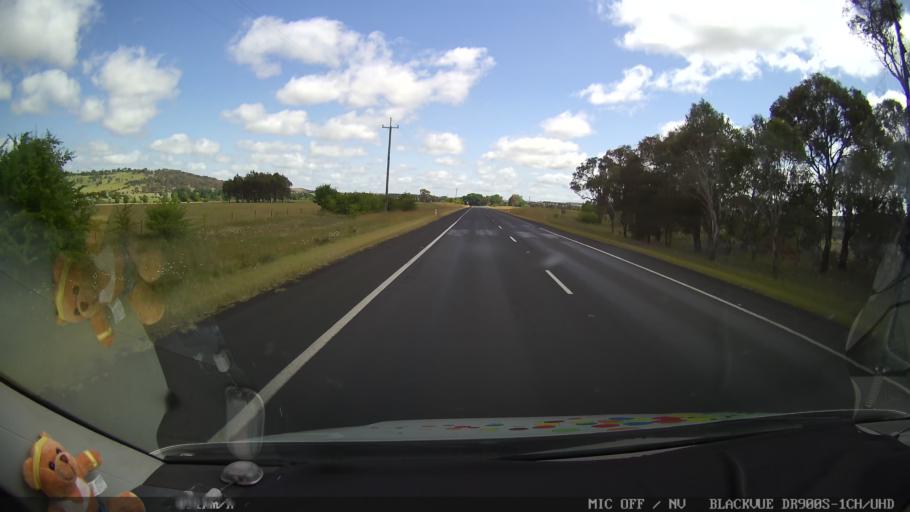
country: AU
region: New South Wales
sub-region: Glen Innes Severn
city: Glen Innes
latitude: -29.8675
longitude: 151.7366
